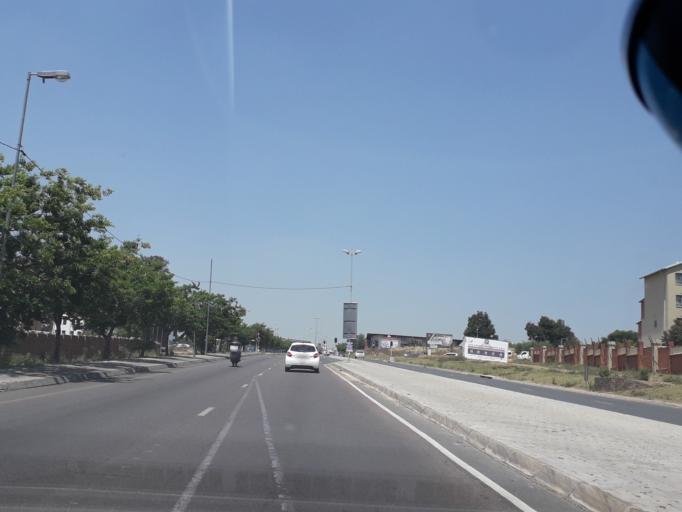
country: ZA
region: Gauteng
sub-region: City of Johannesburg Metropolitan Municipality
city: Midrand
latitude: -25.9723
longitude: 28.1200
